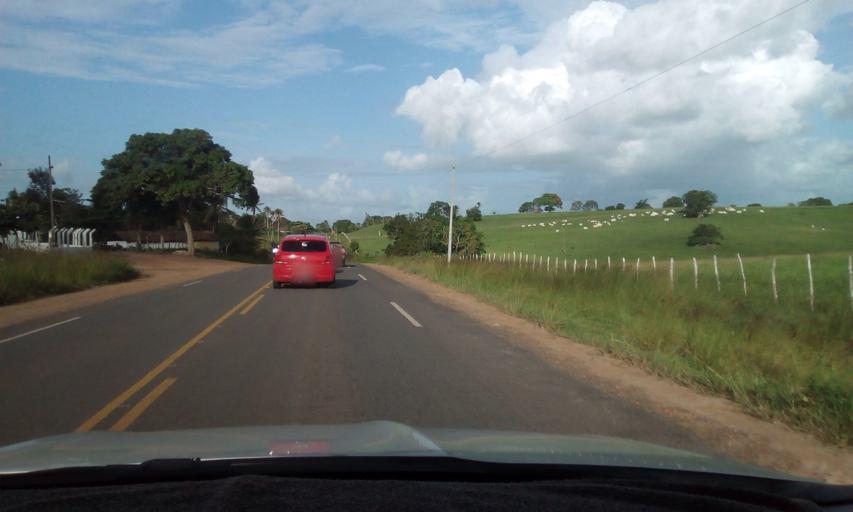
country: BR
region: Paraiba
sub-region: Mamanguape
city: Mamanguape
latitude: -6.8164
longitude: -35.2297
